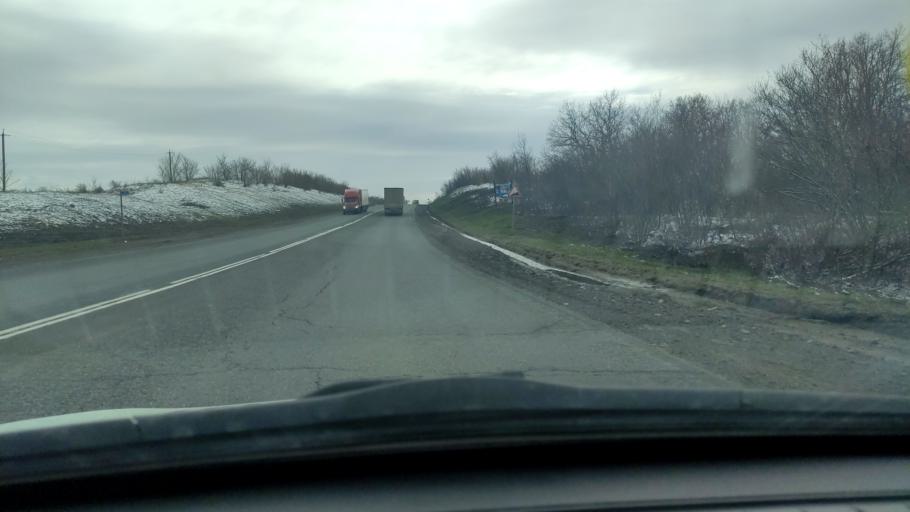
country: RU
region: Samara
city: Zhigulevsk
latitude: 53.3591
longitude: 49.4573
